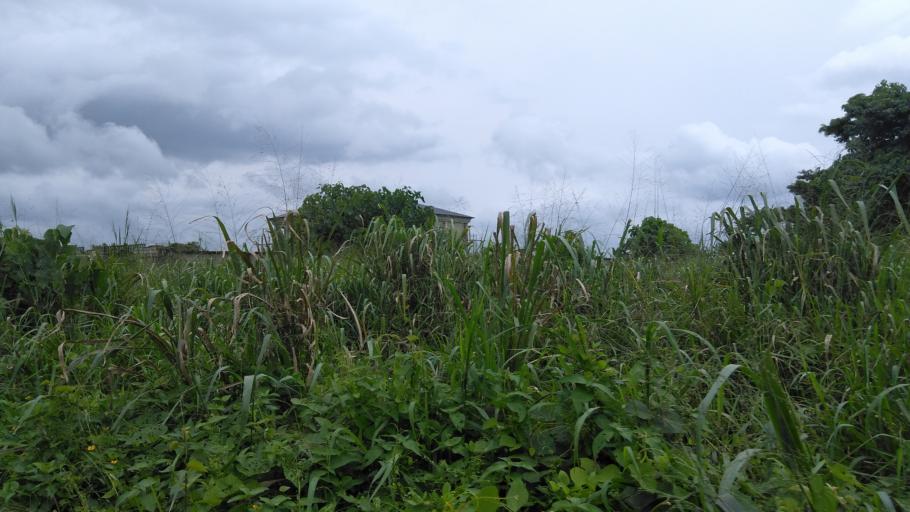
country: NG
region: Ogun
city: Abigi
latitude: 6.6051
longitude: 4.4876
